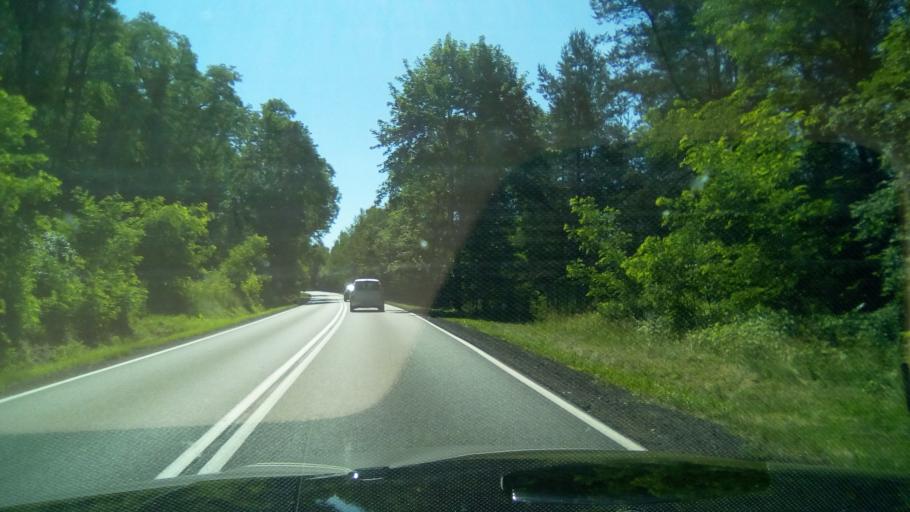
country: PL
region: Lodz Voivodeship
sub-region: Powiat tomaszowski
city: Inowlodz
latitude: 51.5236
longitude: 20.1985
